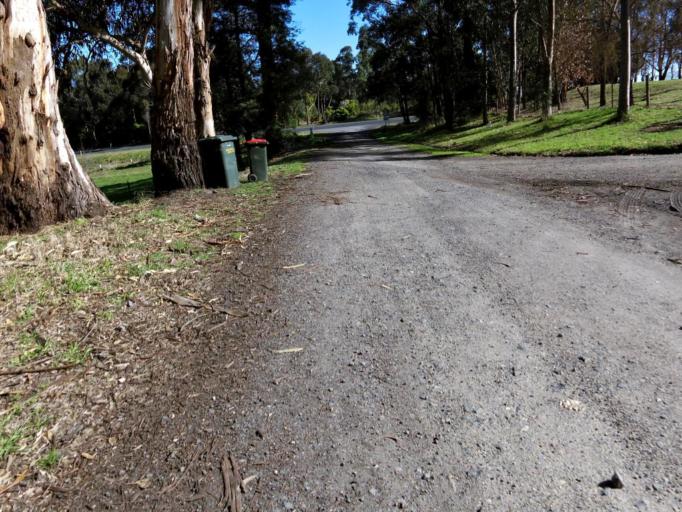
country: AU
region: Victoria
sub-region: Baw Baw
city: Warragul
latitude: -38.0405
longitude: 145.9528
